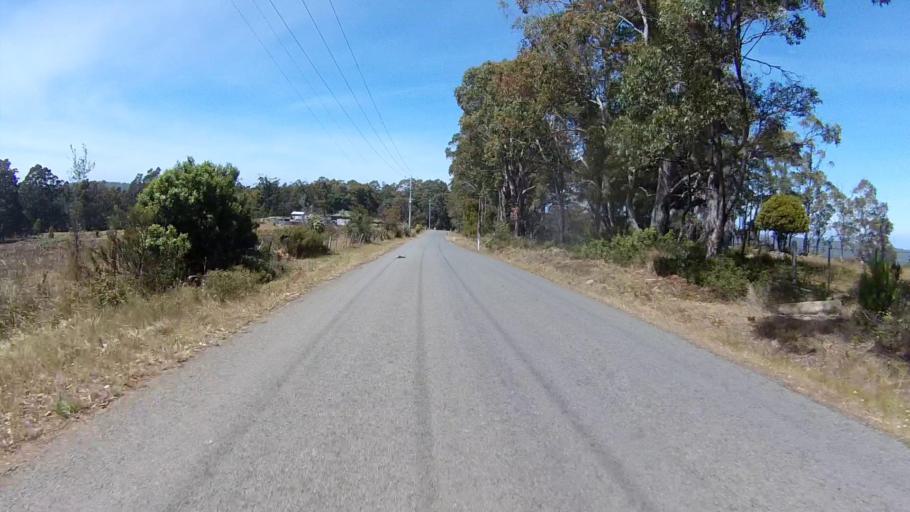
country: AU
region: Tasmania
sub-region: Sorell
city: Sorell
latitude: -42.7343
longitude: 147.7381
